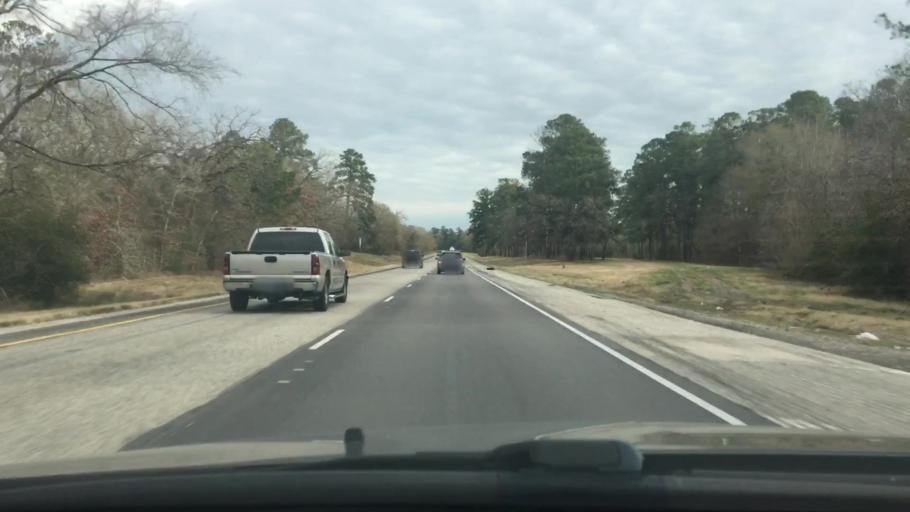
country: US
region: Texas
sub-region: Walker County
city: Huntsville
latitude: 30.8004
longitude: -95.6837
